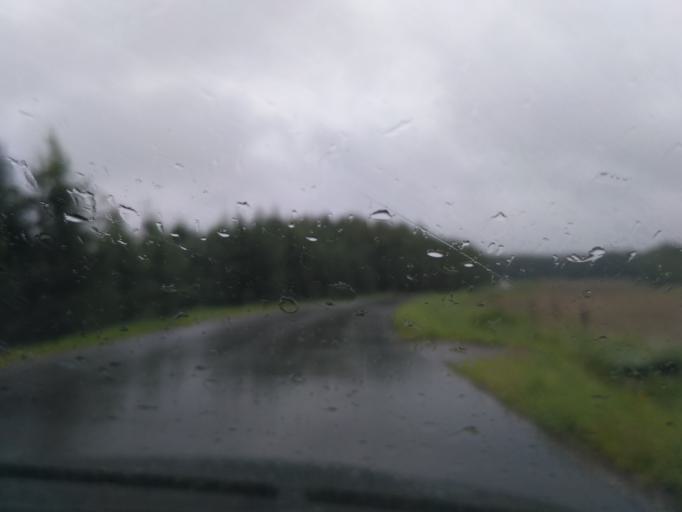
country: PL
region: Subcarpathian Voivodeship
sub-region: Powiat jasielski
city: Debowiec
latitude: 49.6661
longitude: 21.4490
